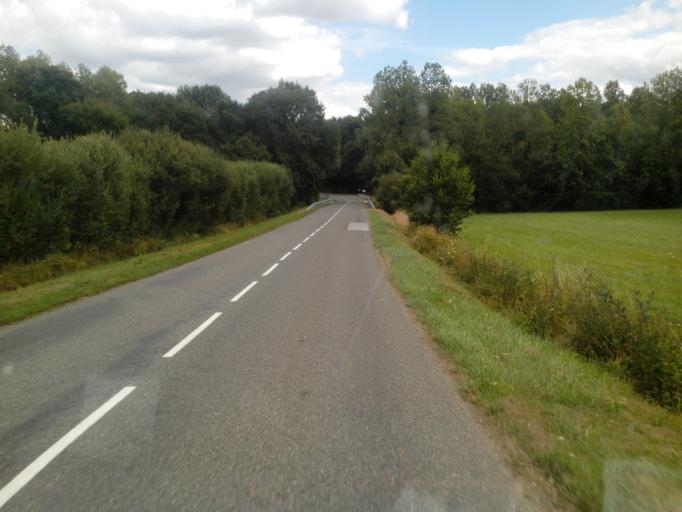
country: FR
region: Brittany
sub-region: Departement du Morbihan
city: Guilliers
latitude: 48.0241
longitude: -2.4450
